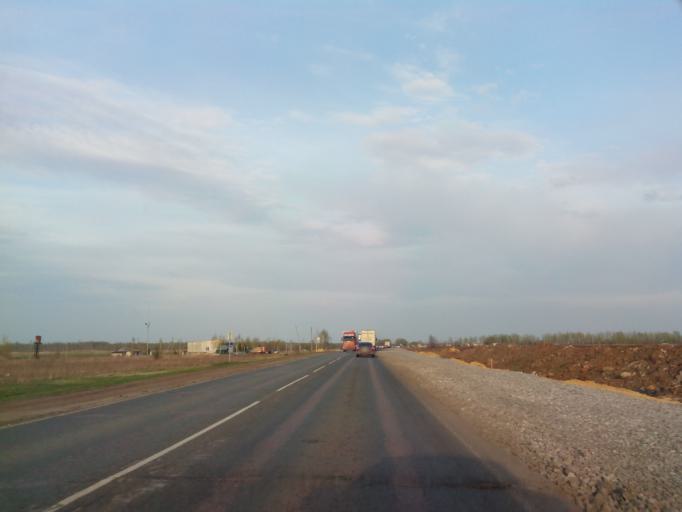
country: RU
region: Rjazan
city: Zarechnyy
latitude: 53.7521
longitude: 39.8350
